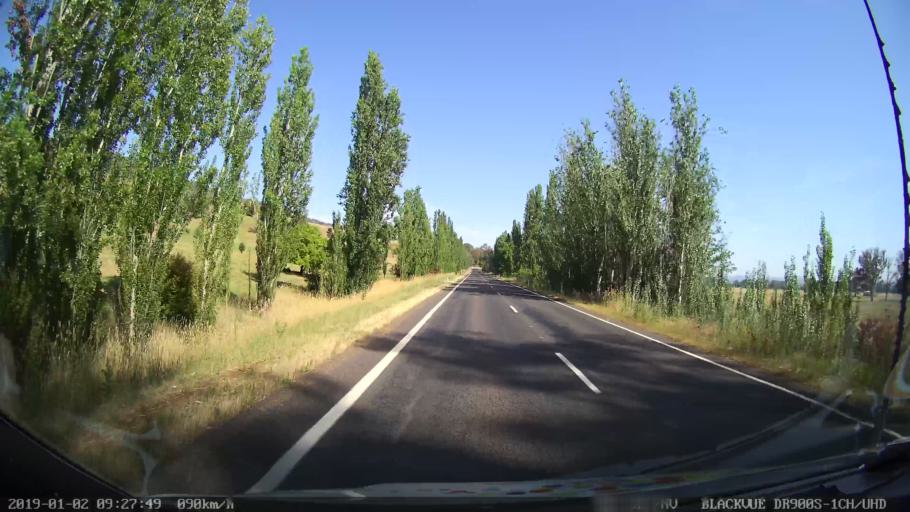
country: AU
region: New South Wales
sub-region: Tumut Shire
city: Tumut
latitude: -35.3578
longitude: 148.2541
